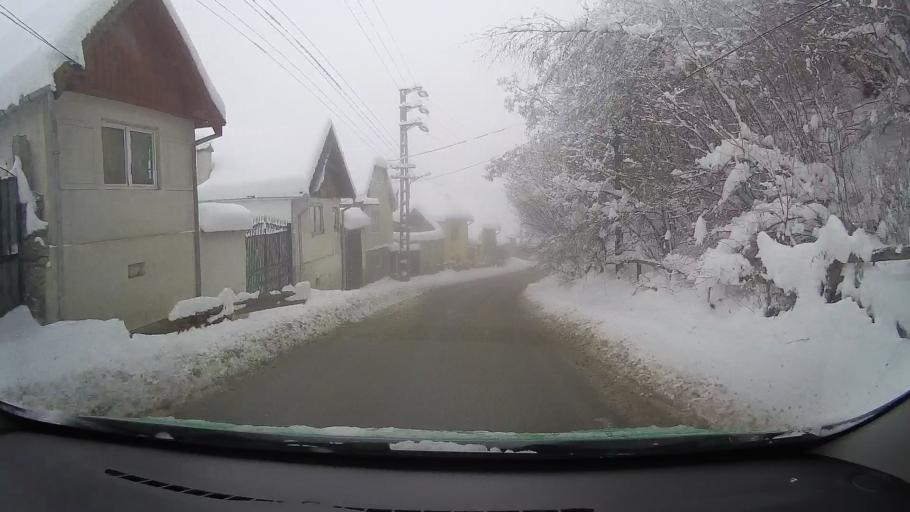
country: RO
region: Sibiu
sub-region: Comuna Poiana Sibiului
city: Poiana Sibiului
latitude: 45.8022
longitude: 23.7772
